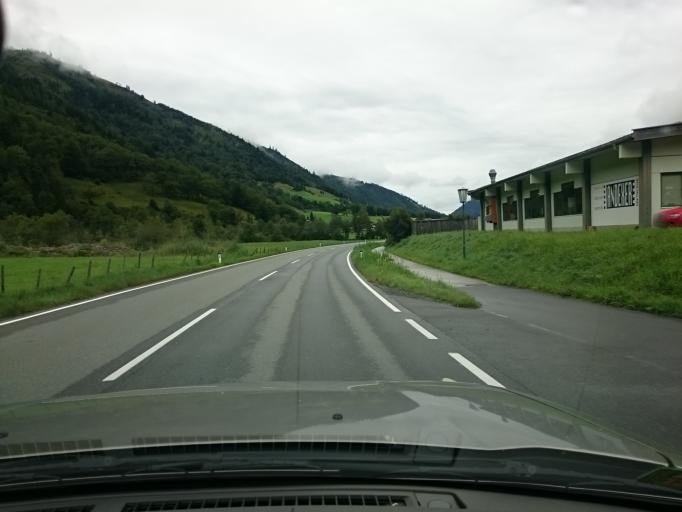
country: AT
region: Salzburg
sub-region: Politischer Bezirk Zell am See
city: Bruck an der Grossglocknerstrasse
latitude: 47.2378
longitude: 12.8248
